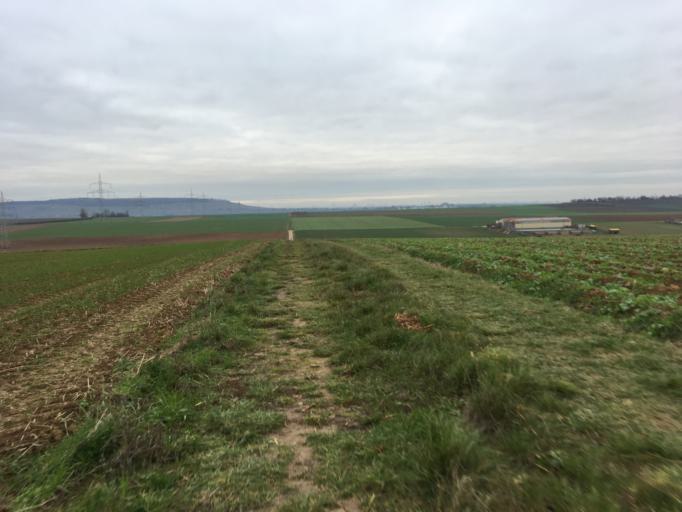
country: DE
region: Baden-Wuerttemberg
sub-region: Regierungsbezirk Stuttgart
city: Nordheim
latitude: 49.0888
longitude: 9.1233
